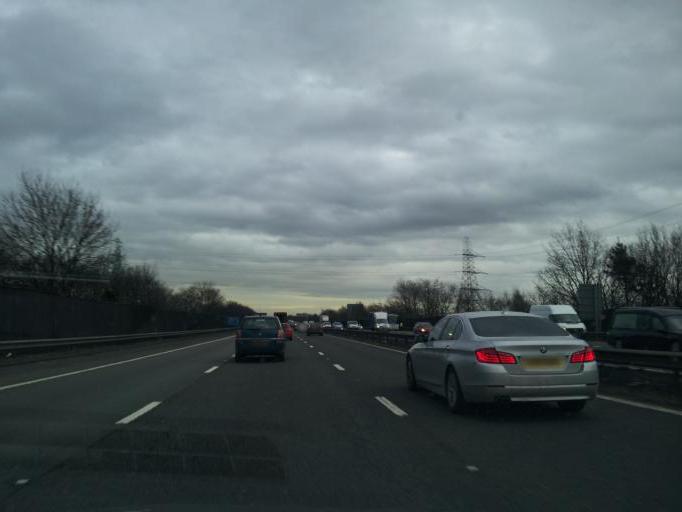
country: GB
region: England
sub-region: Warwickshire
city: Exhall
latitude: 52.4555
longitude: -1.4775
